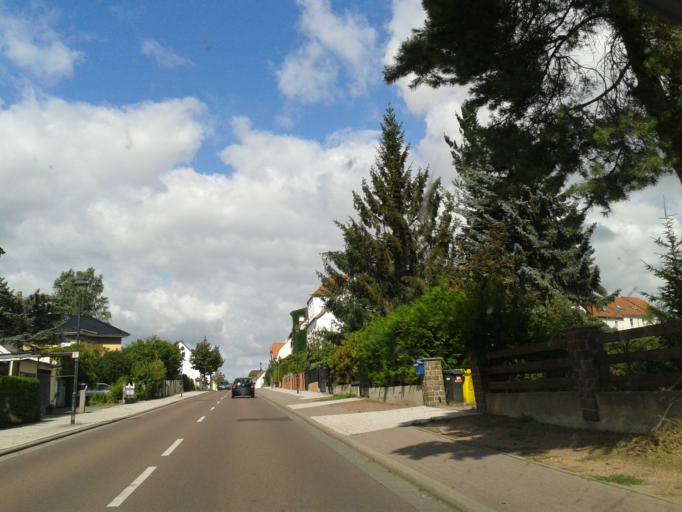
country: DE
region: Saxony-Anhalt
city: Lieskau
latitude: 51.5112
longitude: 11.8958
